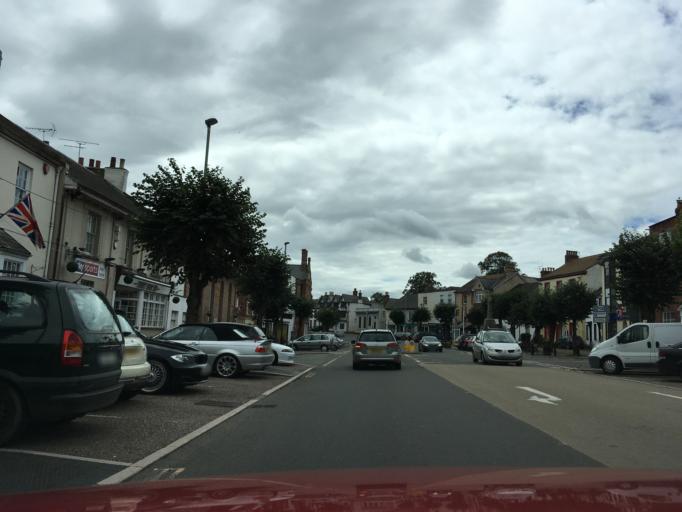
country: GB
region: England
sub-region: Devon
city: Cullompton
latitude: 50.8587
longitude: -3.3923
